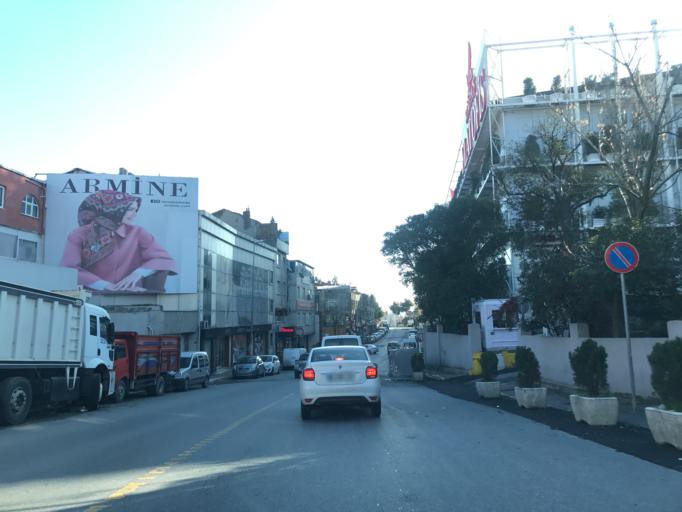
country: TR
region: Istanbul
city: Istanbul
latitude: 41.0386
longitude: 28.9314
